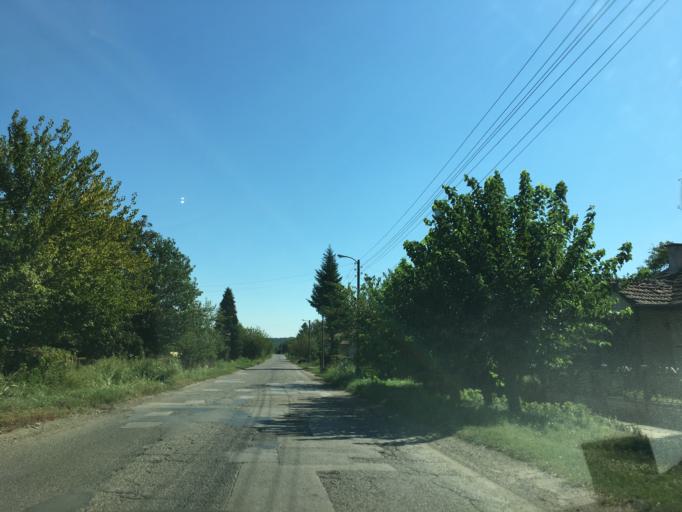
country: RO
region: Dolj
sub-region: Comuna Desa
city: Desa
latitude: 43.7691
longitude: 23.0024
